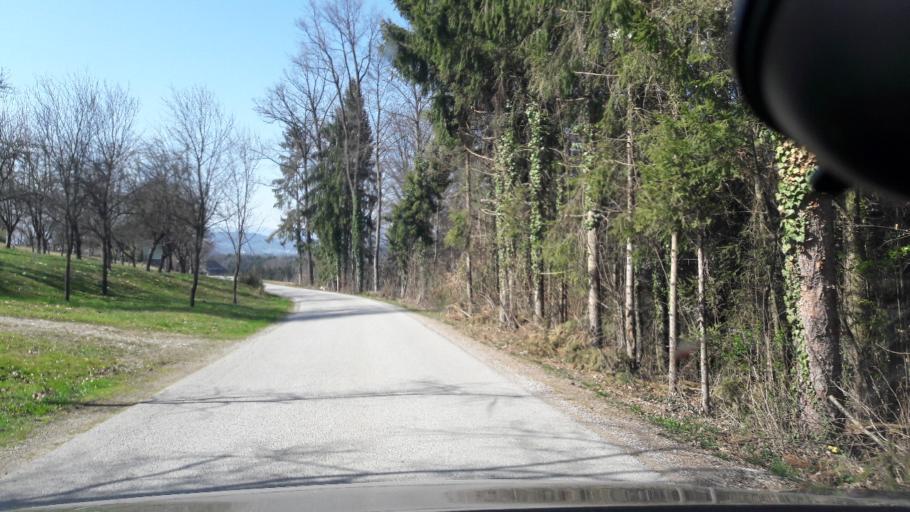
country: AT
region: Styria
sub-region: Politischer Bezirk Graz-Umgebung
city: Attendorf
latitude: 47.0401
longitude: 15.3294
